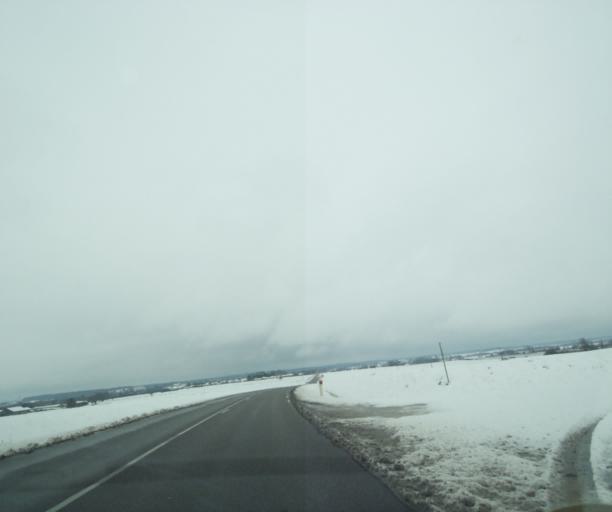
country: FR
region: Champagne-Ardenne
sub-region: Departement de la Haute-Marne
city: Montier-en-Der
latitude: 48.4599
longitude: 4.7520
